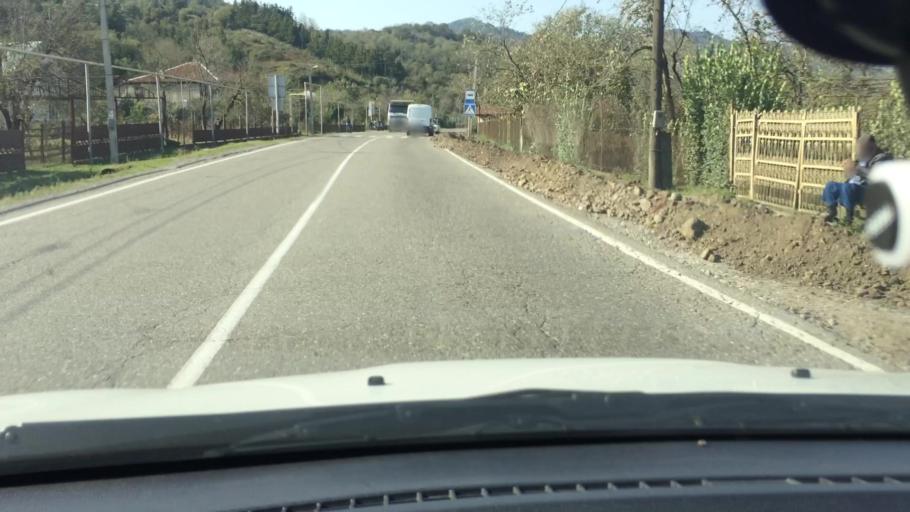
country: GE
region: Guria
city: Lanchkhuti
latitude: 42.0804
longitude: 42.0953
